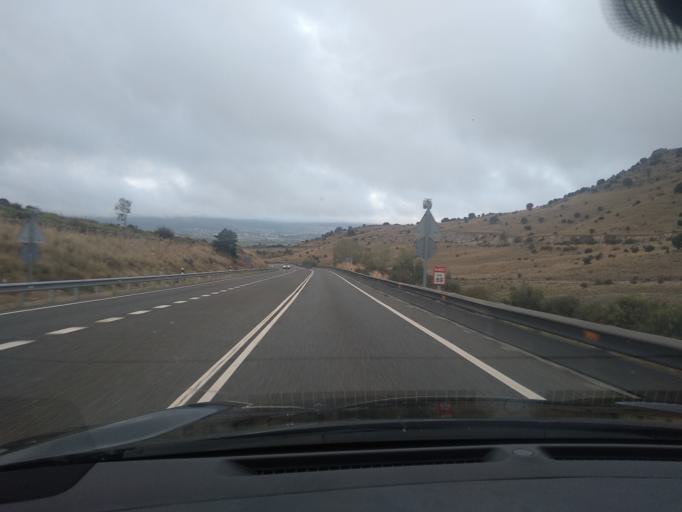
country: ES
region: Castille and Leon
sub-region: Provincia de Segovia
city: Otero de Herreros
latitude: 40.7647
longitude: -4.2082
